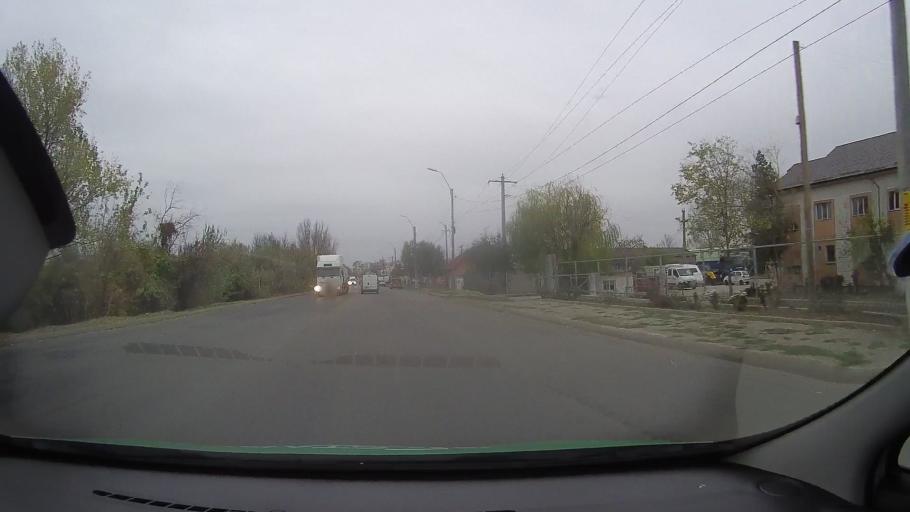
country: RO
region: Ialomita
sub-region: Comuna Slobozia
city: Slobozia
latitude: 44.5760
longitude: 27.3865
